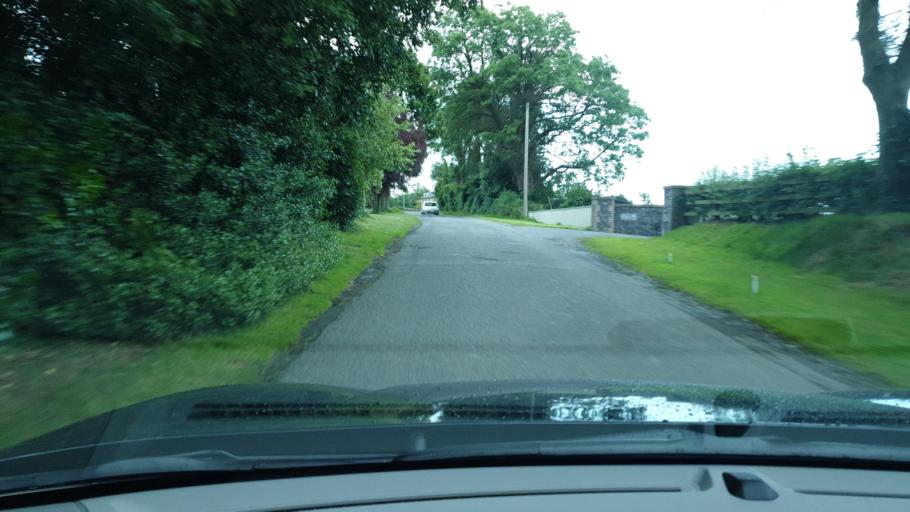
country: IE
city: Kentstown
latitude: 53.5943
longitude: -6.5790
